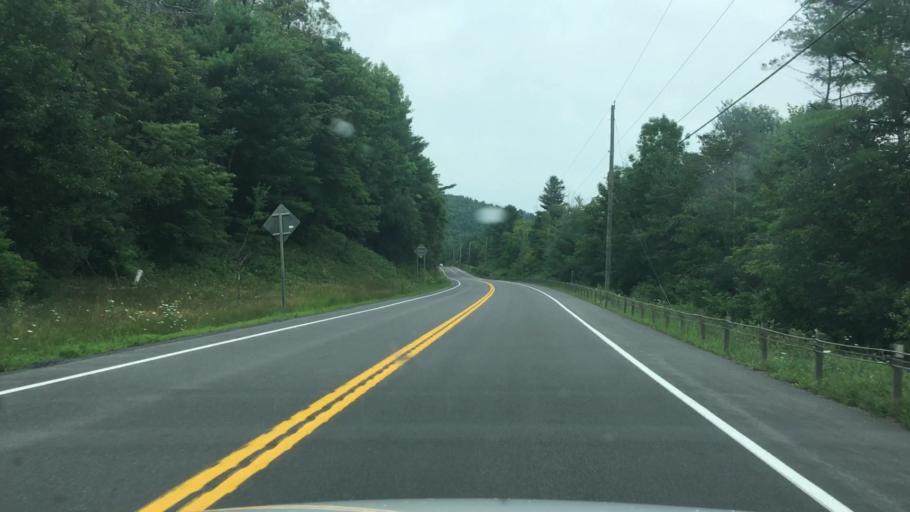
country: US
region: New York
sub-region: Essex County
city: Keeseville
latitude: 44.4693
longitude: -73.5716
